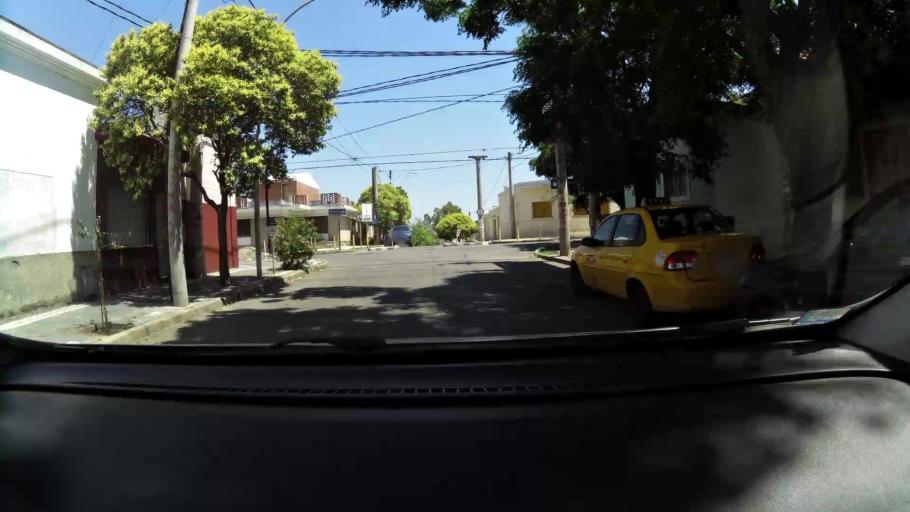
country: AR
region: Cordoba
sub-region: Departamento de Capital
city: Cordoba
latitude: -31.4023
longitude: -64.2008
